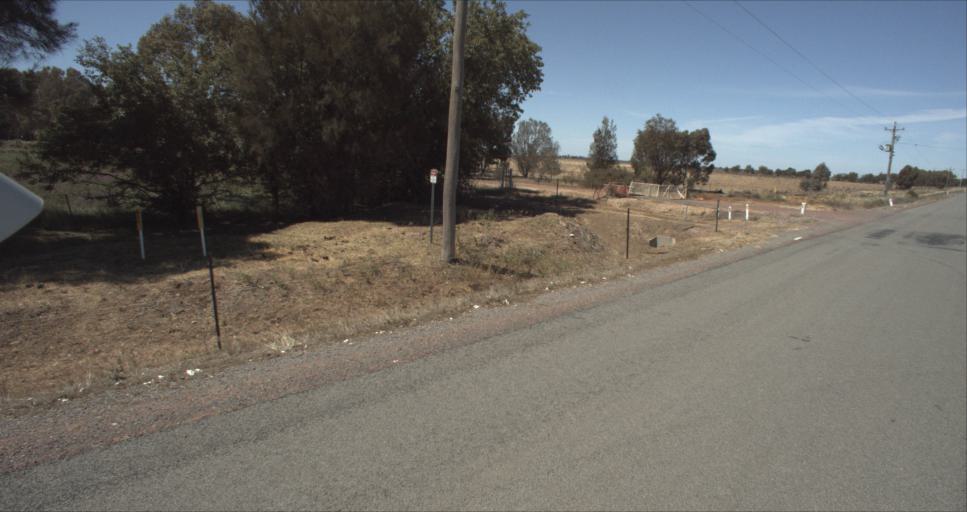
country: AU
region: New South Wales
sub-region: Leeton
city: Leeton
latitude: -34.4308
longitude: 146.2996
